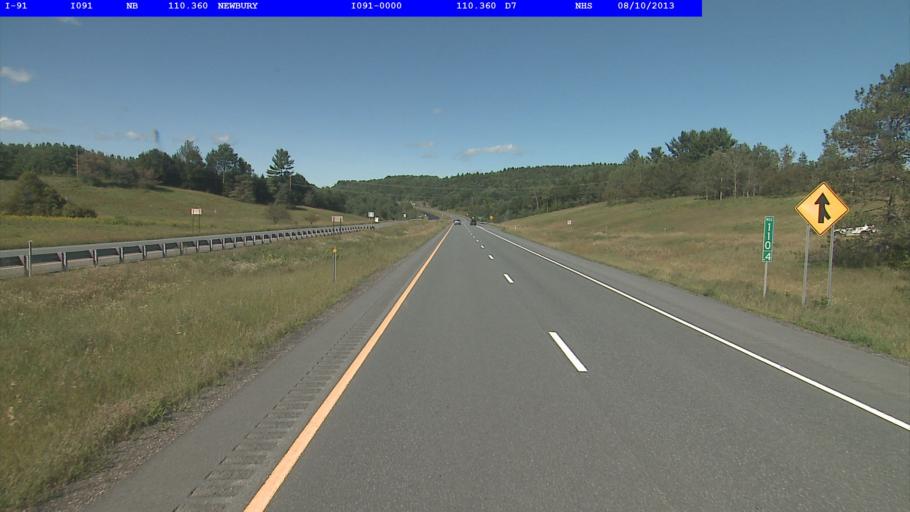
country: US
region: New Hampshire
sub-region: Grafton County
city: Woodsville
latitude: 44.1603
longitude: -72.0882
